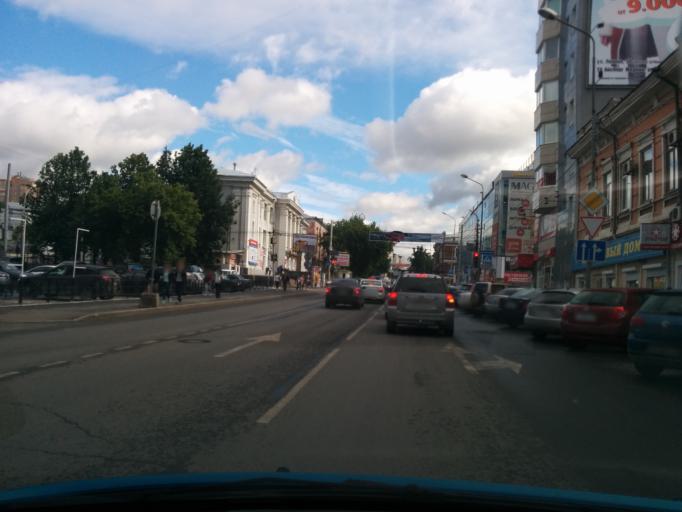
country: RU
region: Perm
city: Perm
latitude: 58.0086
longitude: 56.2352
